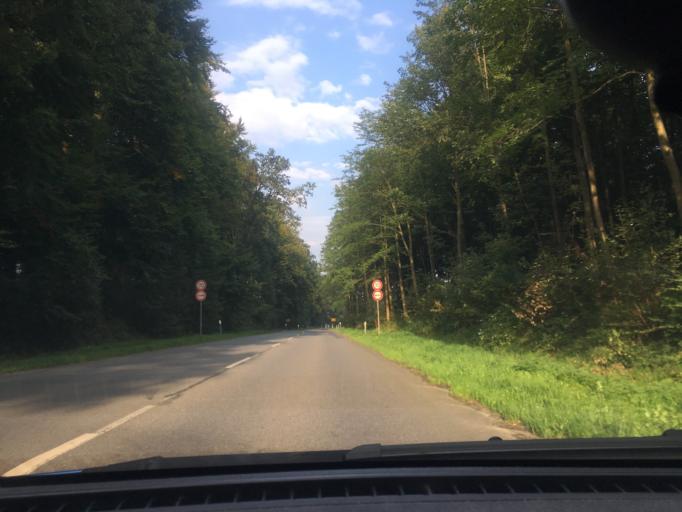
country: DE
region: Lower Saxony
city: Scharnebeck
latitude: 53.2842
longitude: 10.4939
